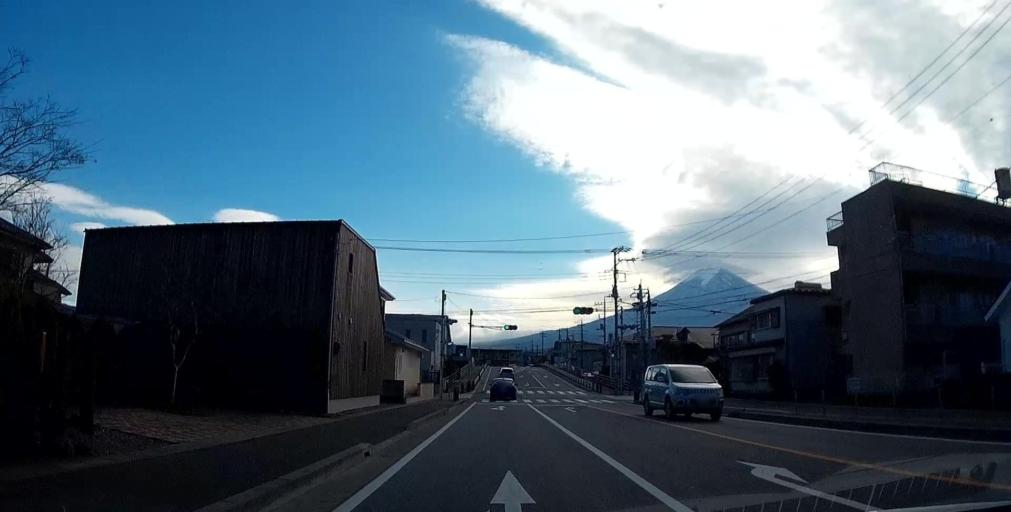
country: JP
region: Yamanashi
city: Fujikawaguchiko
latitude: 35.4925
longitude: 138.7934
